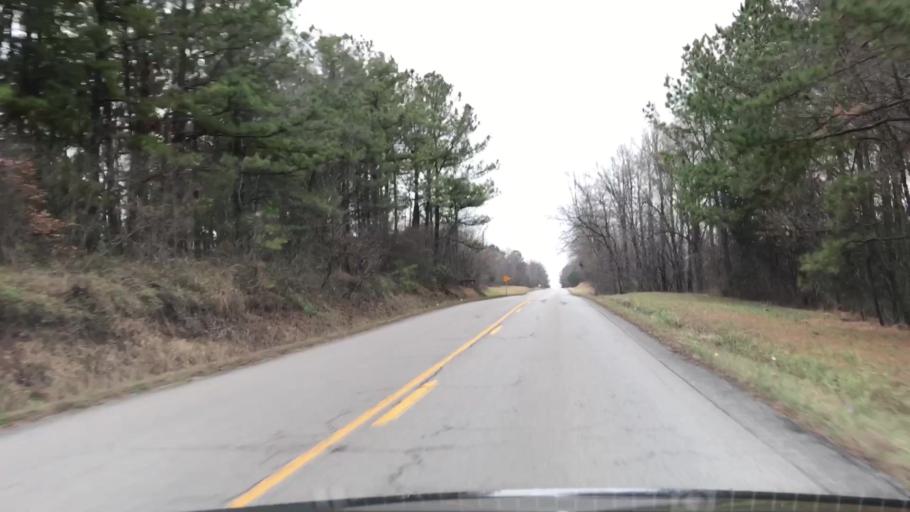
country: US
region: Kentucky
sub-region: Muhlenberg County
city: Morehead
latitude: 37.2786
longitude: -87.2086
